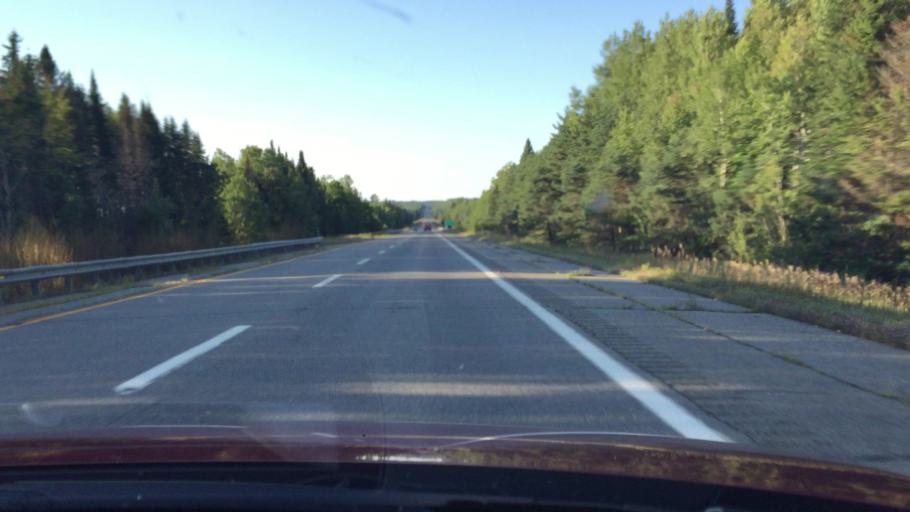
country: US
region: Maine
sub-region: Penobscot County
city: Patten
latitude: 45.8086
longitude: -68.4281
